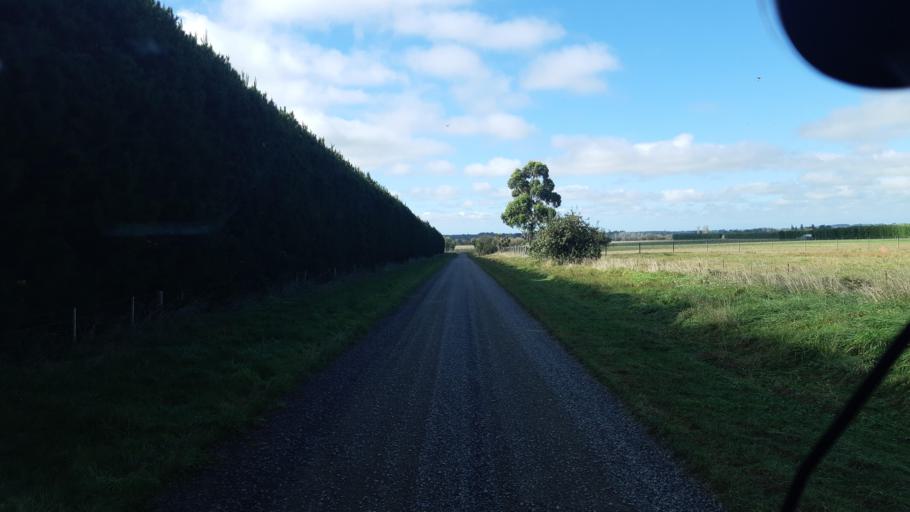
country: NZ
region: Canterbury
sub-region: Waimakariri District
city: Oxford
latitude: -43.2110
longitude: 172.4037
